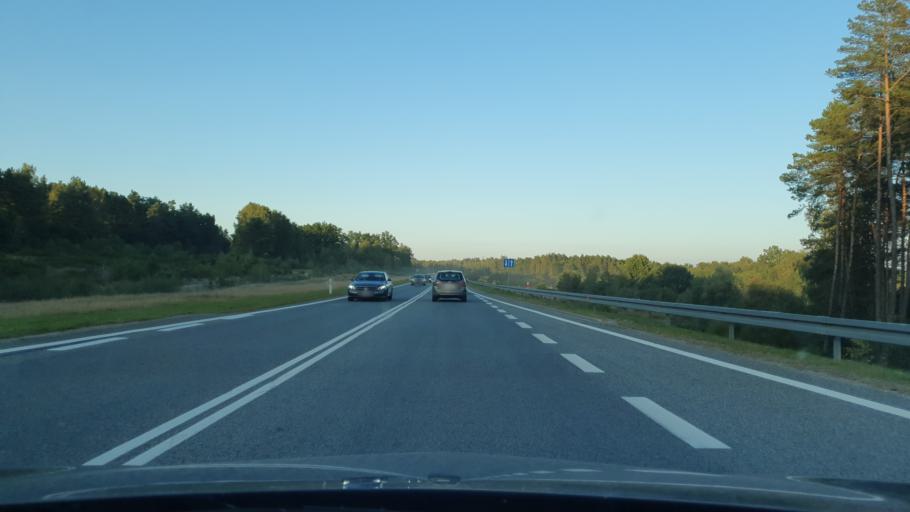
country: PL
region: Pomeranian Voivodeship
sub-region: Slupsk
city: Slupsk
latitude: 54.4350
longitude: 17.0646
